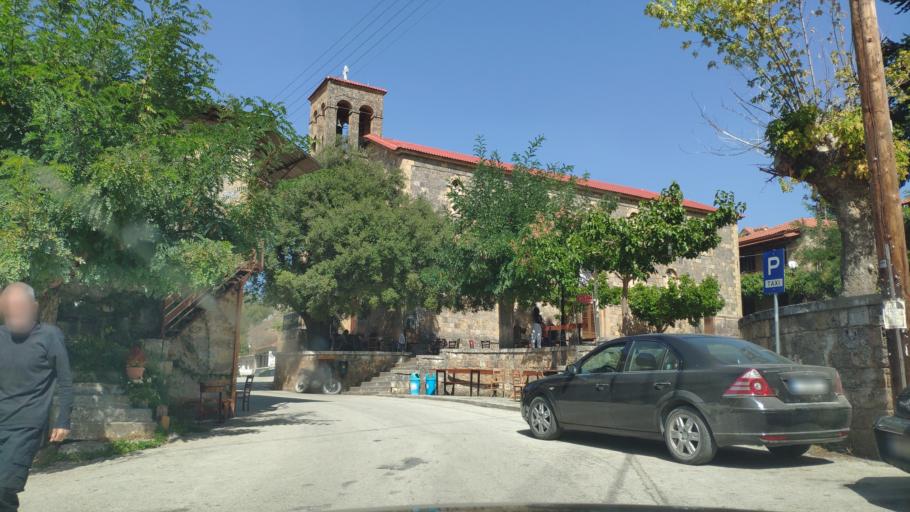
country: GR
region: West Greece
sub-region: Nomos Achaias
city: Aiyira
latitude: 37.9333
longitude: 22.3407
